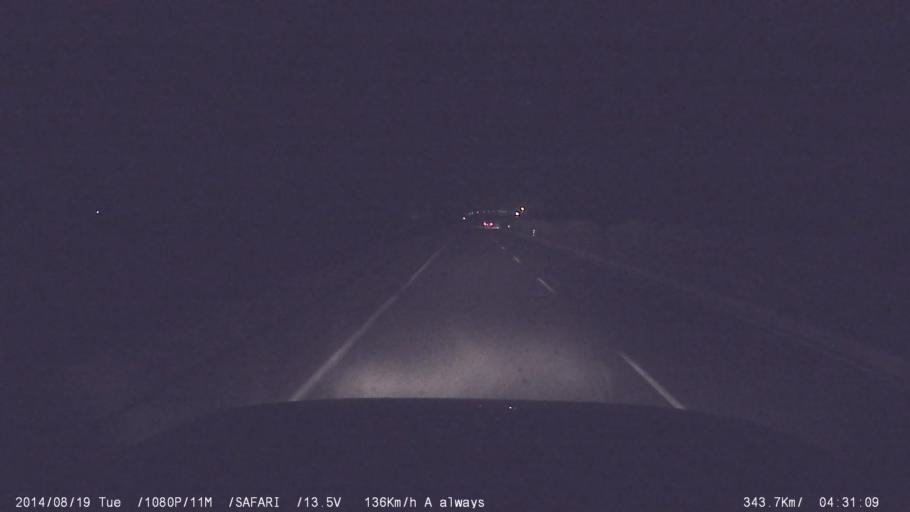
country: IN
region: Tamil Nadu
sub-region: Erode
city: Perundurai
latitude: 11.2768
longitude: 77.5560
